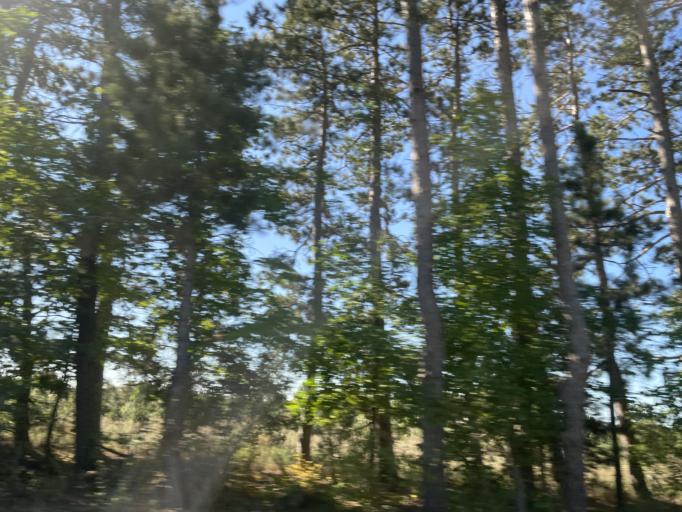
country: US
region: Michigan
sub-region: Benzie County
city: Beulah
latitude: 44.6173
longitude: -86.0668
